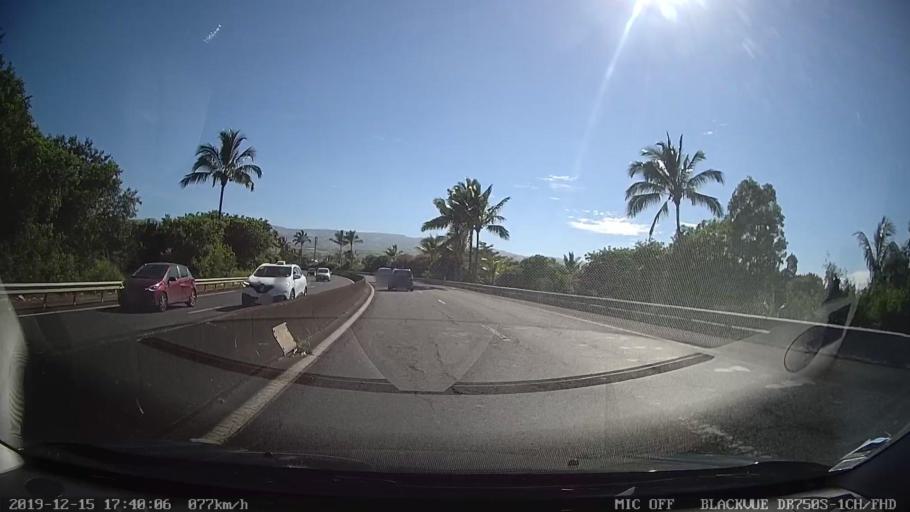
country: RE
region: Reunion
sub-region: Reunion
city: Saint-Pierre
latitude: -21.3228
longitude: 55.4865
